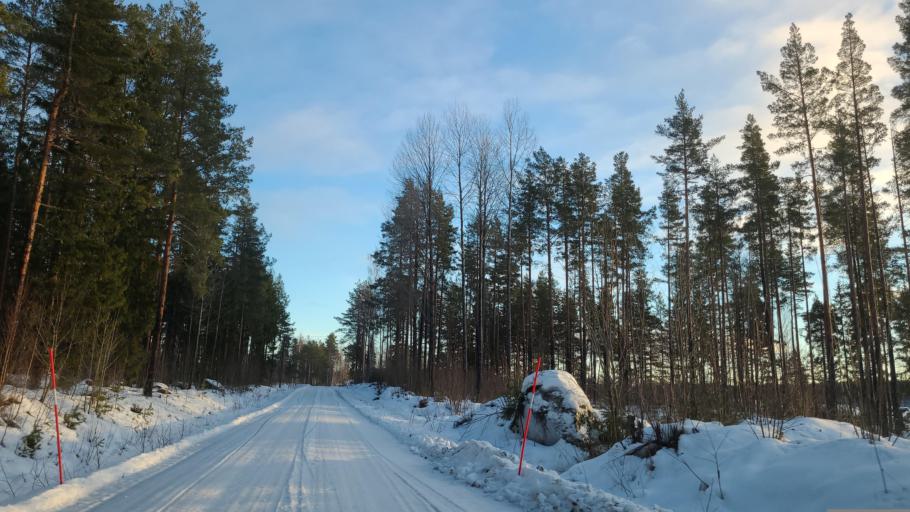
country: SE
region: Gaevleborg
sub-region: Bollnas Kommun
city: Kilafors
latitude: 61.3995
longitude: 16.6534
